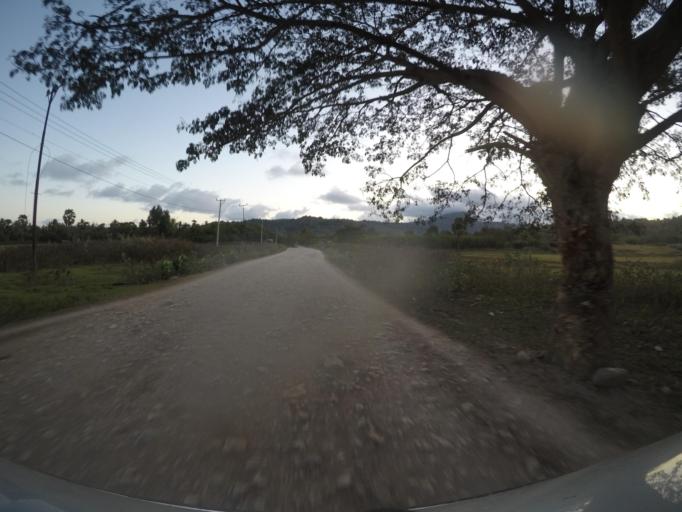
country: TL
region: Viqueque
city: Viqueque
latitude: -8.7713
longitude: 126.6412
